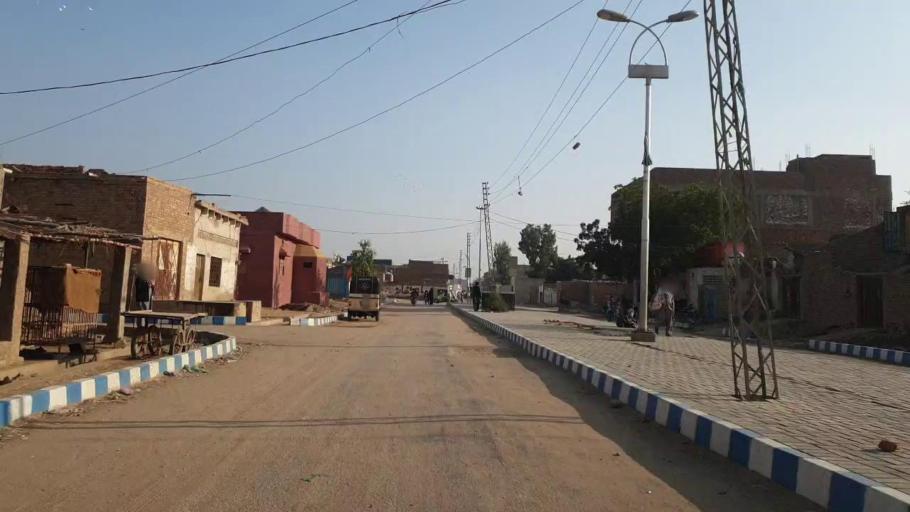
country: PK
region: Sindh
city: Kotri
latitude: 25.3601
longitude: 68.2612
